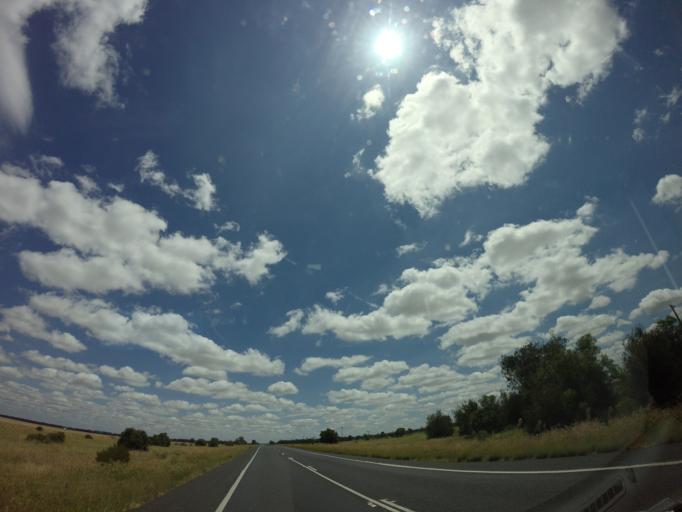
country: AU
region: New South Wales
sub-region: Moree Plains
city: Moree
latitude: -29.1546
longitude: 150.0169
